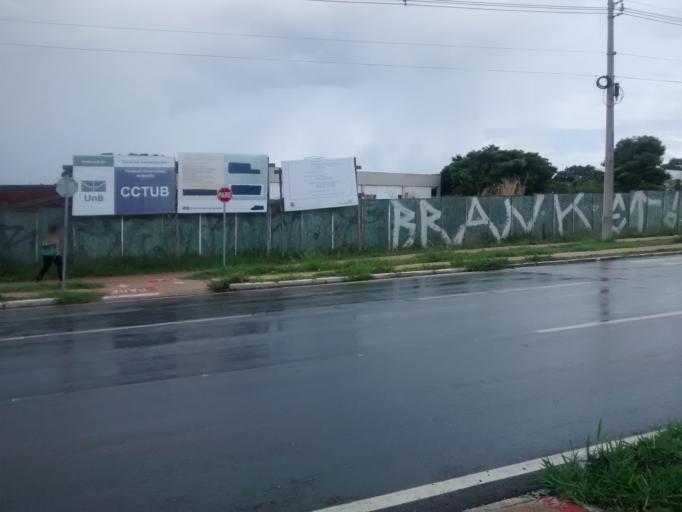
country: BR
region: Federal District
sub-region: Brasilia
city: Brasilia
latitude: -15.7663
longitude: -47.8733
